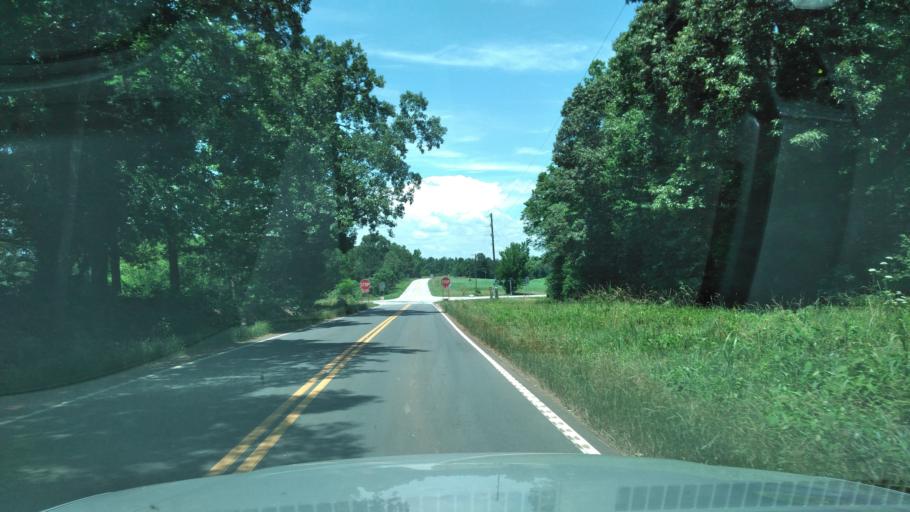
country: US
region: South Carolina
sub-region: Greenwood County
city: Ware Shoals
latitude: 34.4306
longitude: -82.1403
